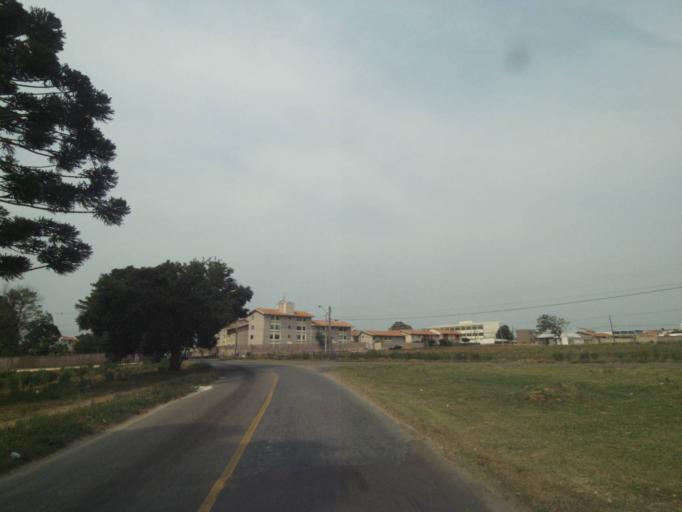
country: BR
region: Parana
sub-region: Sao Jose Dos Pinhais
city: Sao Jose dos Pinhais
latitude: -25.5266
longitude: -49.2766
